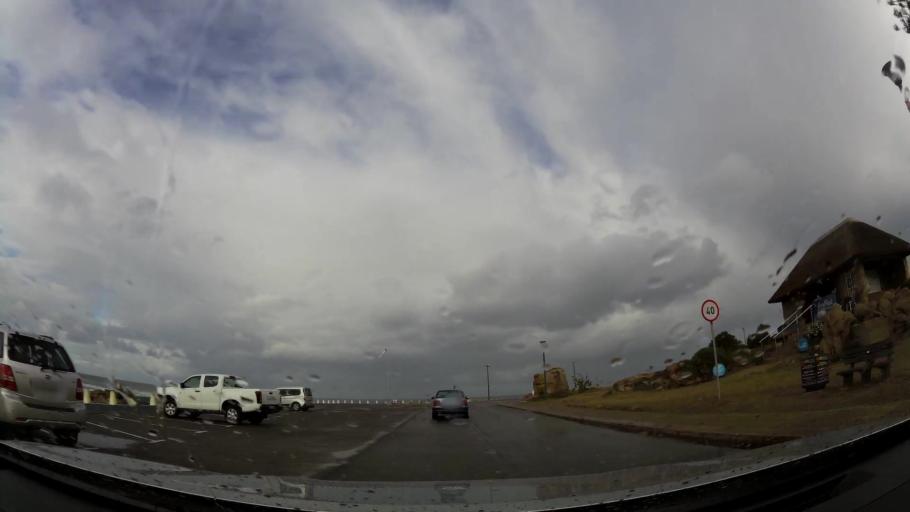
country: ZA
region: Western Cape
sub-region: Eden District Municipality
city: Mossel Bay
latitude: -34.1850
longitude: 22.1593
